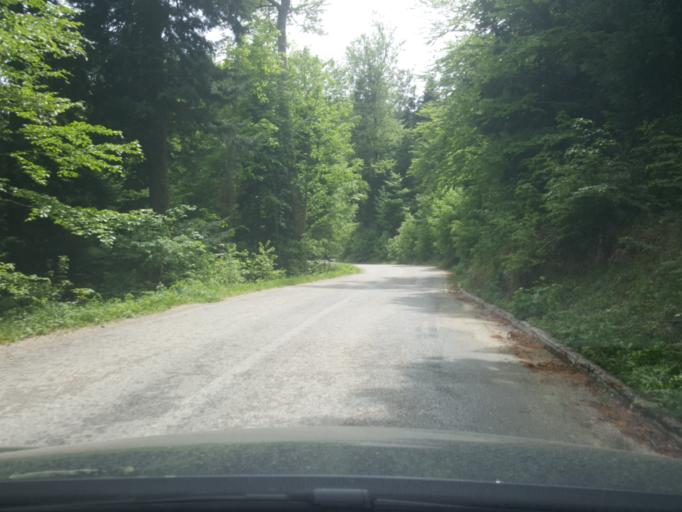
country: RS
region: Central Serbia
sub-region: Zlatiborski Okrug
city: Bajina Basta
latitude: 43.9152
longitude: 19.4936
